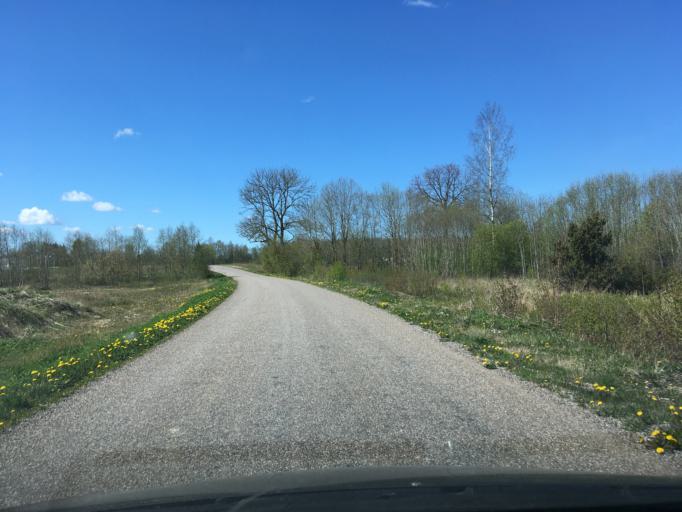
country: EE
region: Harju
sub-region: Rae vald
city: Vaida
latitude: 59.1983
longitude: 25.0562
